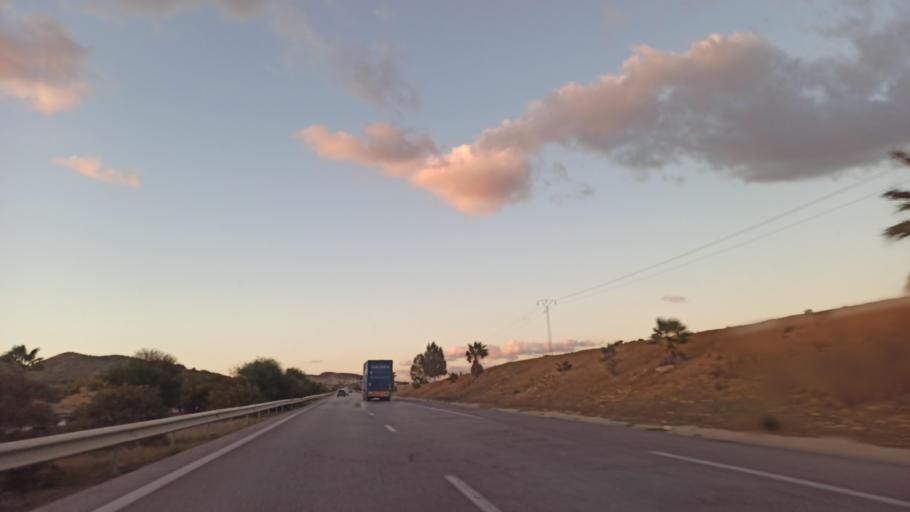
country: TN
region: Susah
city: Harqalah
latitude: 36.2212
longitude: 10.4175
